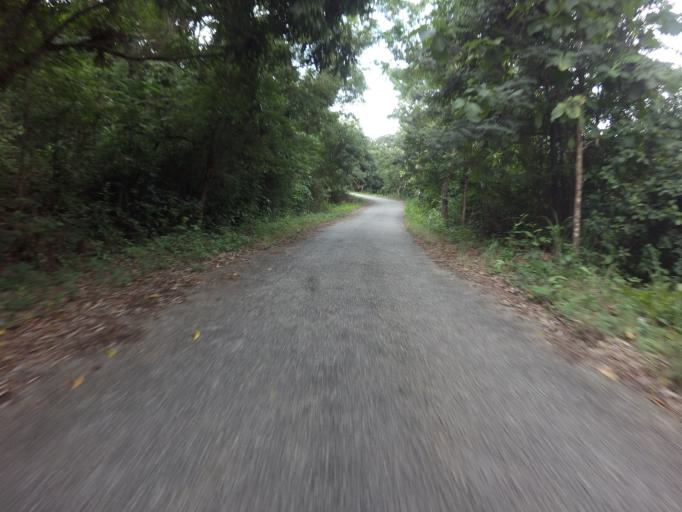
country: TG
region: Plateaux
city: Kpalime
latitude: 6.8818
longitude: 0.4451
